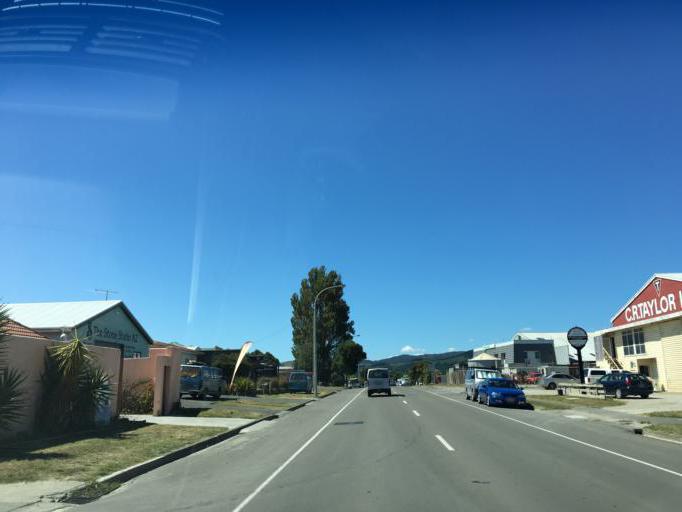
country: NZ
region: Gisborne
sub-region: Gisborne District
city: Gisborne
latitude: -38.6682
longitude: 178.0042
